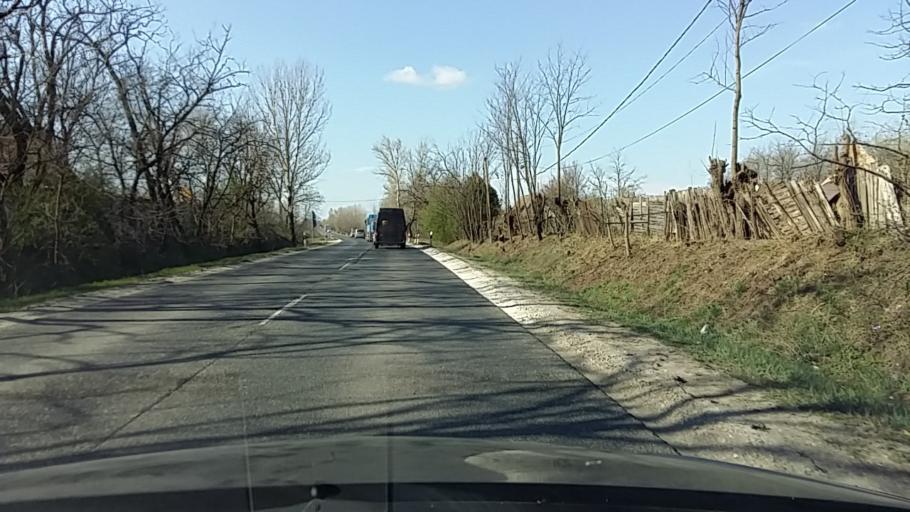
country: HU
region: Pest
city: Felsopakony
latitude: 47.3429
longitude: 19.2048
